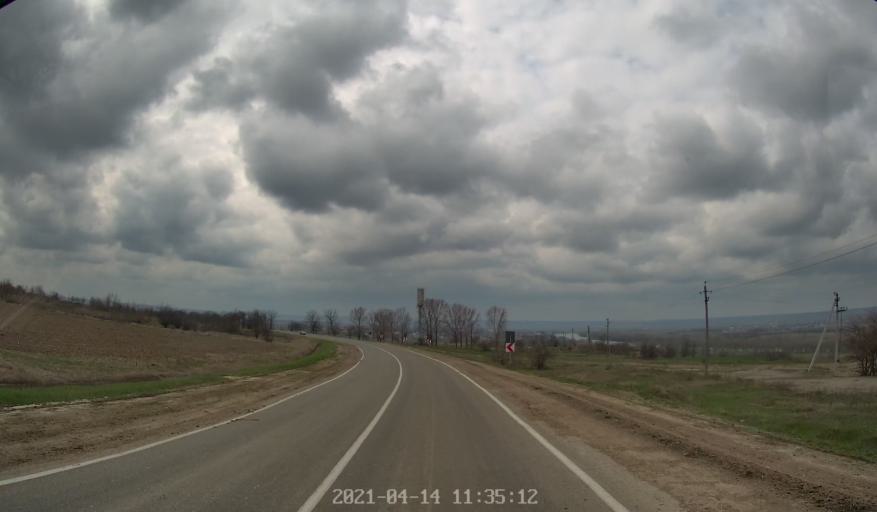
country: MD
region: Criuleni
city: Criuleni
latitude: 47.1717
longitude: 29.1643
